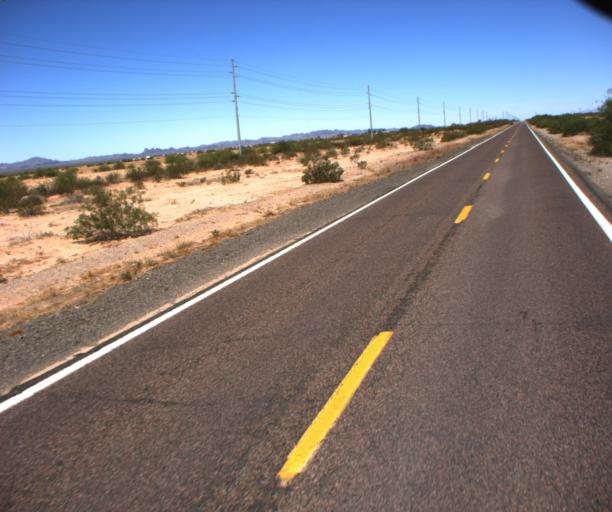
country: US
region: Arizona
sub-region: La Paz County
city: Salome
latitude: 33.8456
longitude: -113.8967
